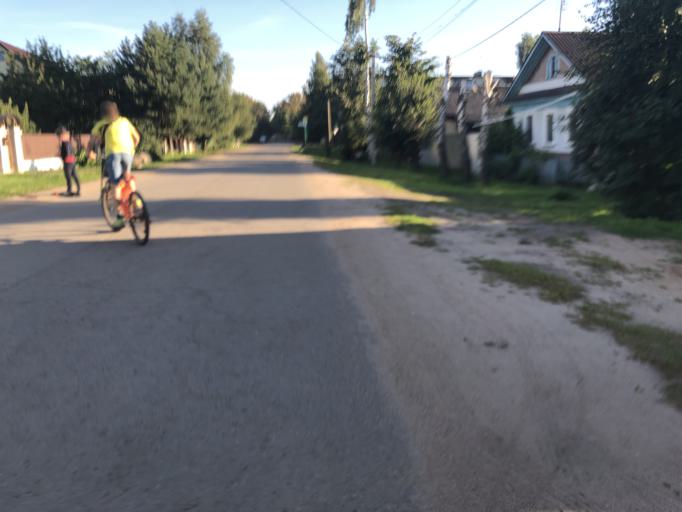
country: RU
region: Tverskaya
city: Rzhev
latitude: 56.2444
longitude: 34.3344
